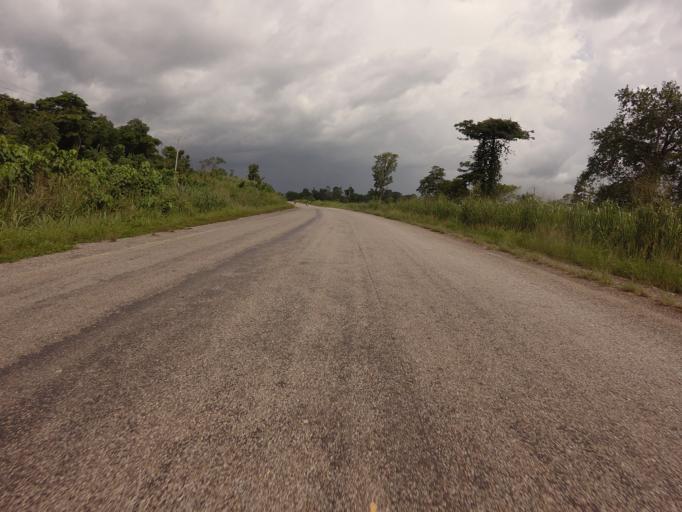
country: TG
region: Plateaux
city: Badou
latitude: 7.7352
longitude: 0.5291
